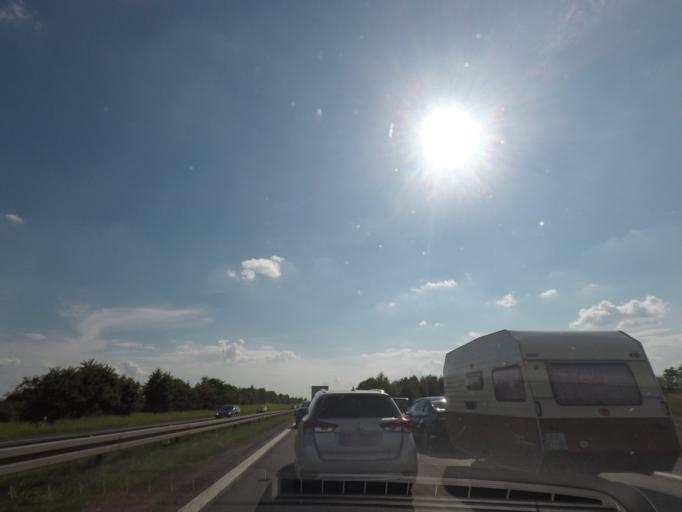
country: PL
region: Silesian Voivodeship
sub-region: Powiat czestochowski
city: Koscielec
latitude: 50.9040
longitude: 19.2018
